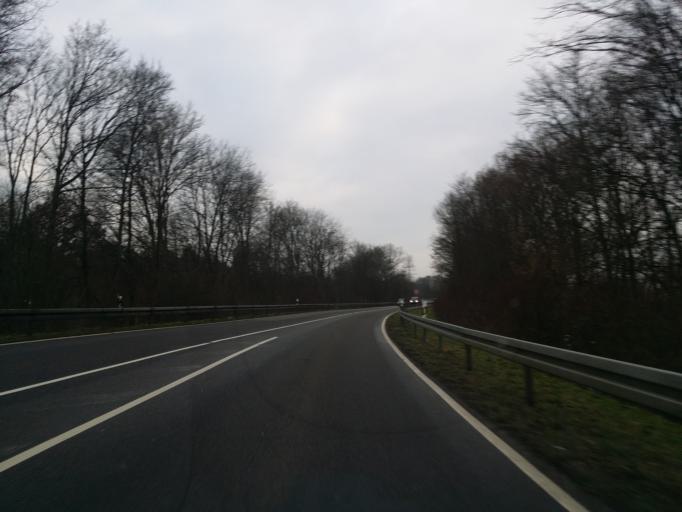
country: DE
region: Hesse
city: Eppstein
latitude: 50.1424
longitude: 8.3603
